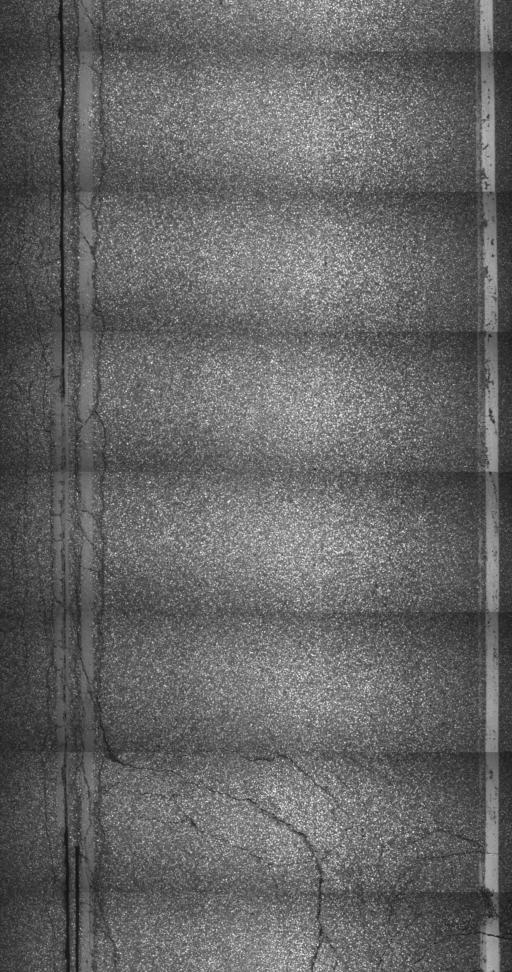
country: US
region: Vermont
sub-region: Windsor County
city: Chester
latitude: 43.3580
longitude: -72.7954
